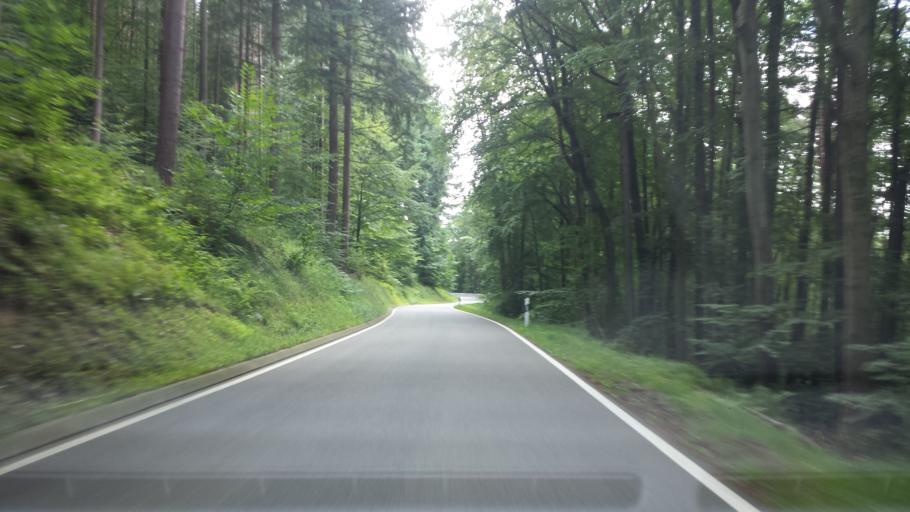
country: DE
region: Rheinland-Pfalz
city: Ramberg
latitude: 49.2738
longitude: 8.0127
